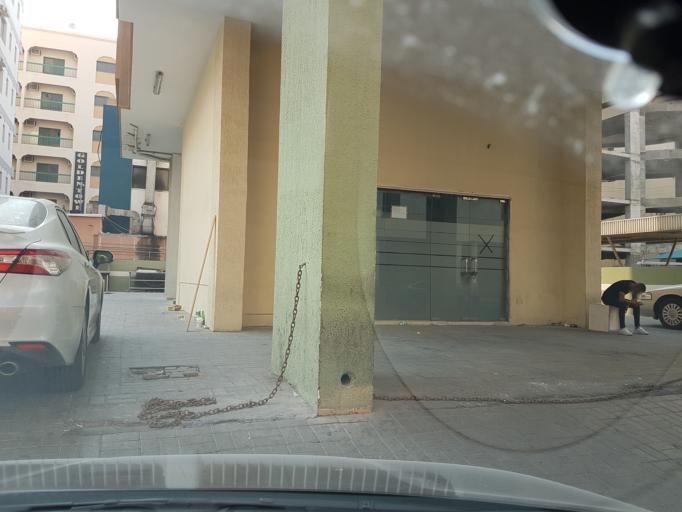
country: BH
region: Manama
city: Manama
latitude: 26.2328
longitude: 50.5971
